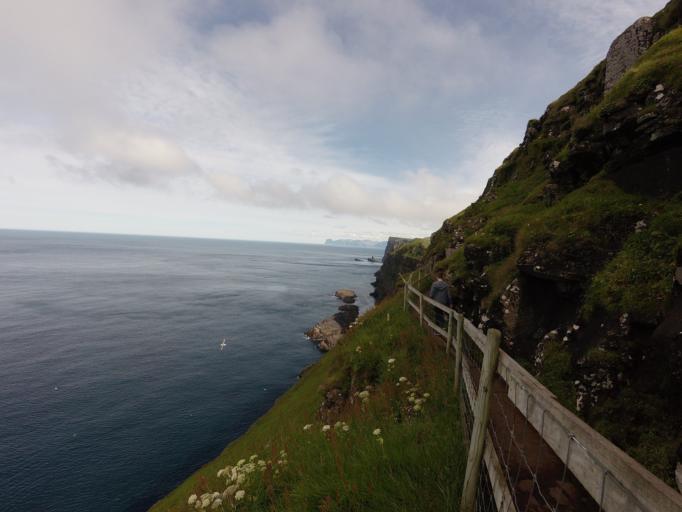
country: FO
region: Vagar
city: Sorvagur
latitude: 62.1027
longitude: -7.6607
